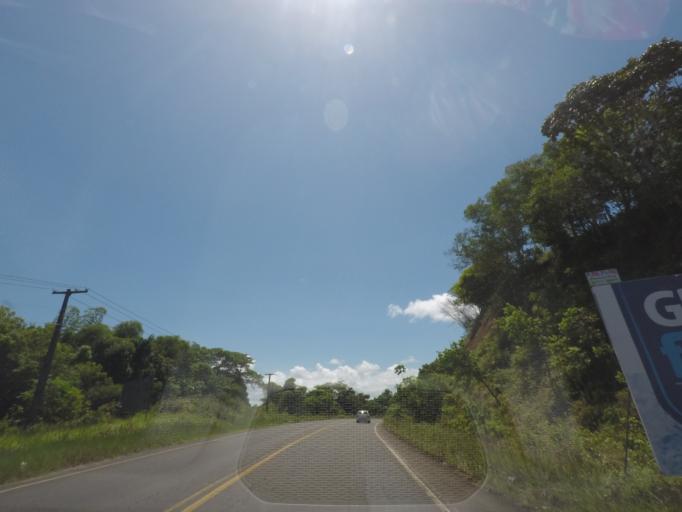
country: BR
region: Bahia
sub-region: Valenca
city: Valenca
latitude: -13.3283
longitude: -39.0486
